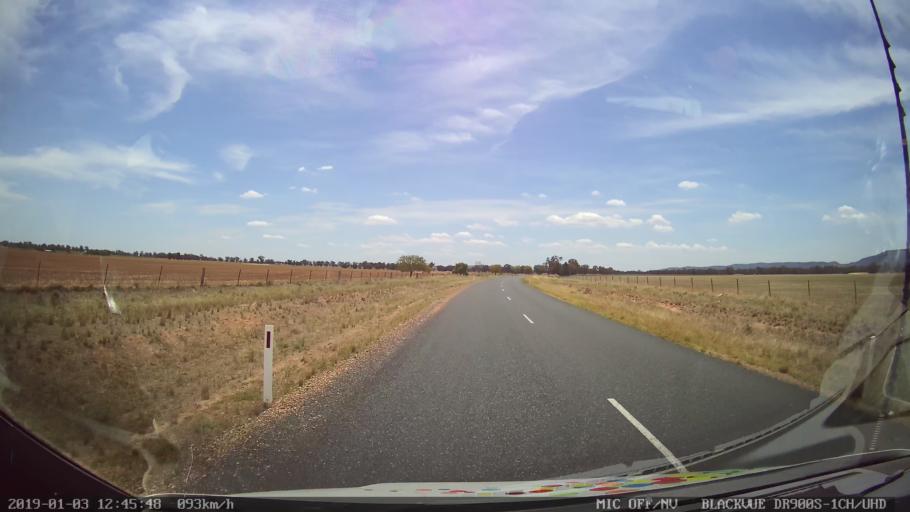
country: AU
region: New South Wales
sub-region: Weddin
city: Grenfell
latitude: -33.7449
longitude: 148.2263
